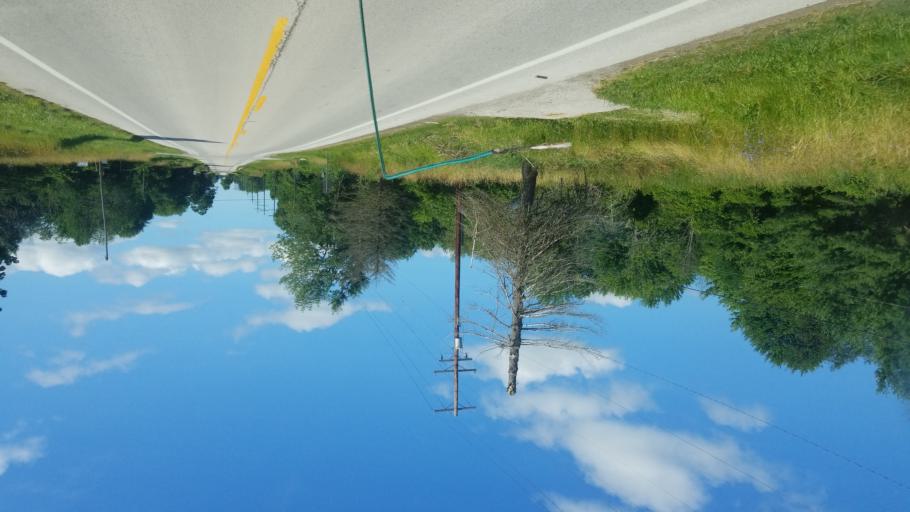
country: US
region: Ohio
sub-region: Ashtabula County
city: Conneaut
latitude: 41.8179
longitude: -80.5722
